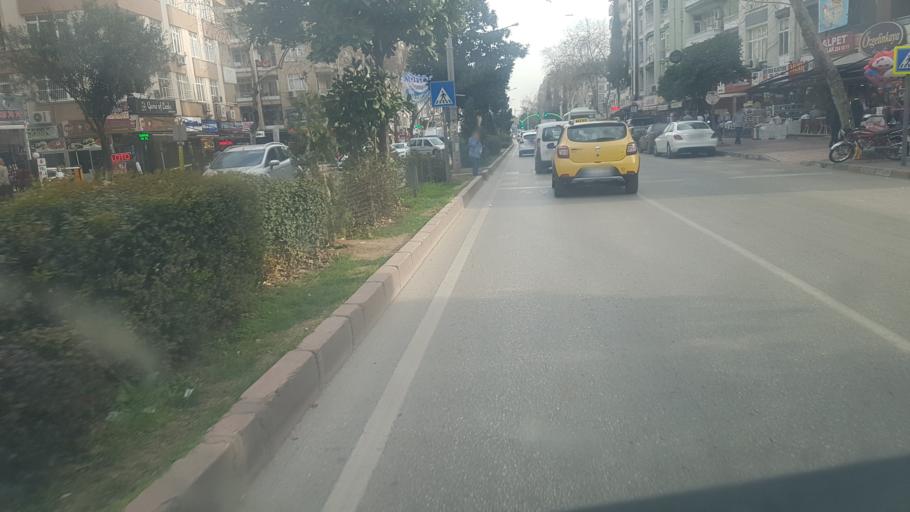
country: TR
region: Adana
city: Adana
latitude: 37.0244
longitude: 35.3147
